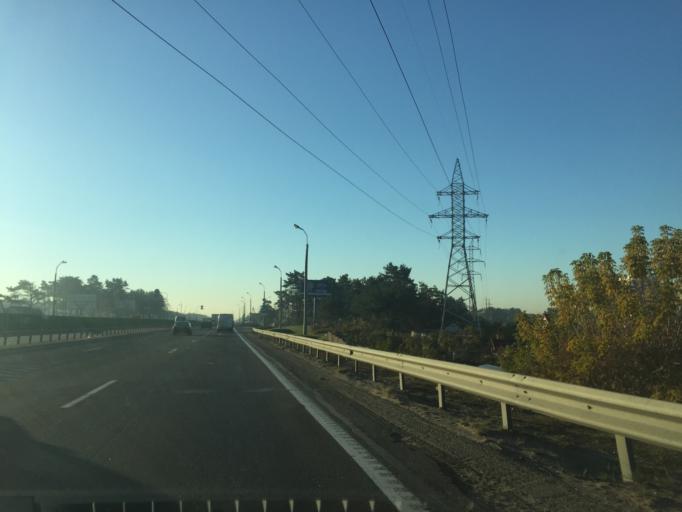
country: BY
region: Minsk
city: Vyaliki Trastsyanets
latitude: 53.9181
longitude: 27.6824
